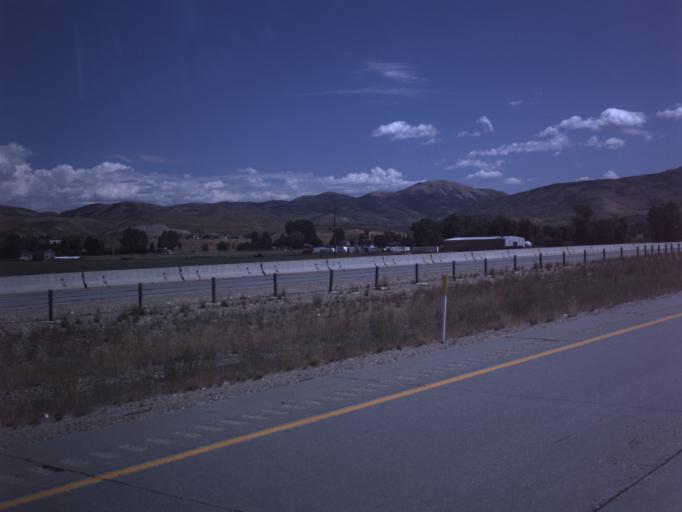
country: US
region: Utah
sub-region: Morgan County
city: Mountain Green
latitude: 41.1383
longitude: -111.8080
